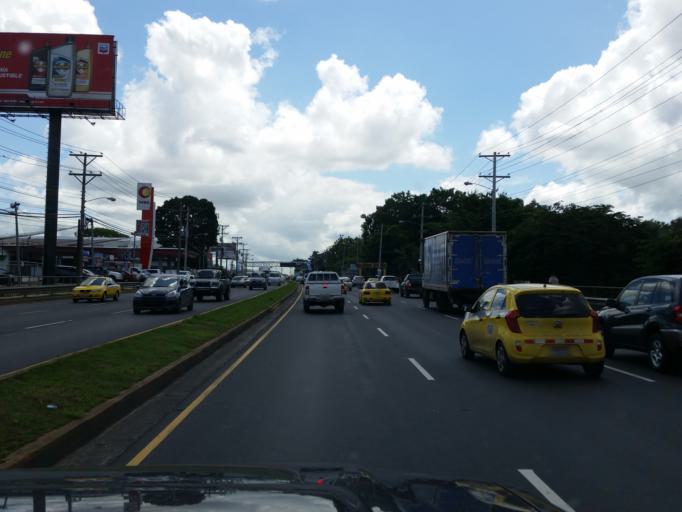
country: PA
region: Panama
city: San Miguelito
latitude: 9.0509
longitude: -79.4482
